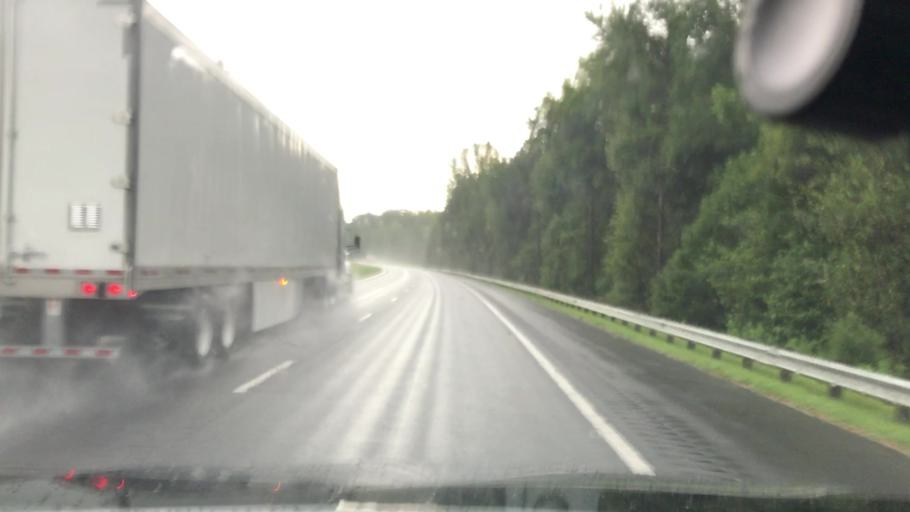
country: US
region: North Carolina
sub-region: Iredell County
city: Statesville
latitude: 35.9756
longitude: -80.8380
